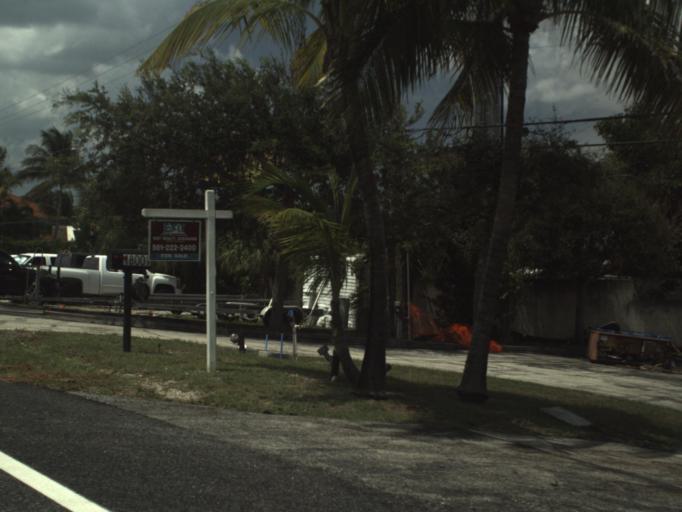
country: US
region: Florida
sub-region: Palm Beach County
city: Tequesta
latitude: 26.9851
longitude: -80.0922
